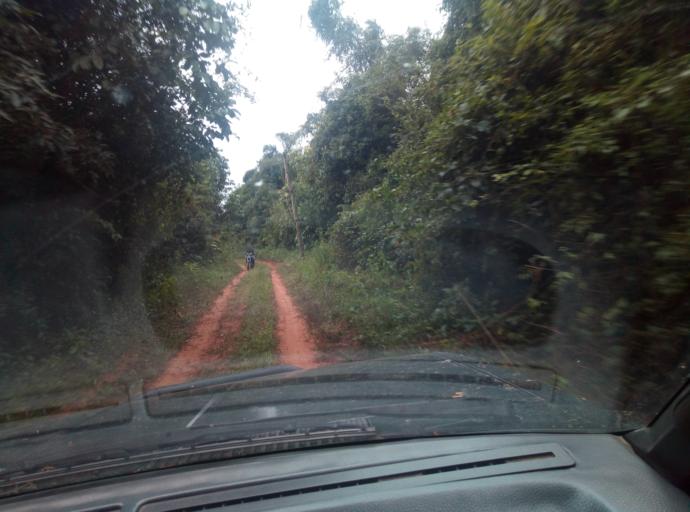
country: PY
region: Caaguazu
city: Carayao
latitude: -25.1901
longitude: -56.3450
